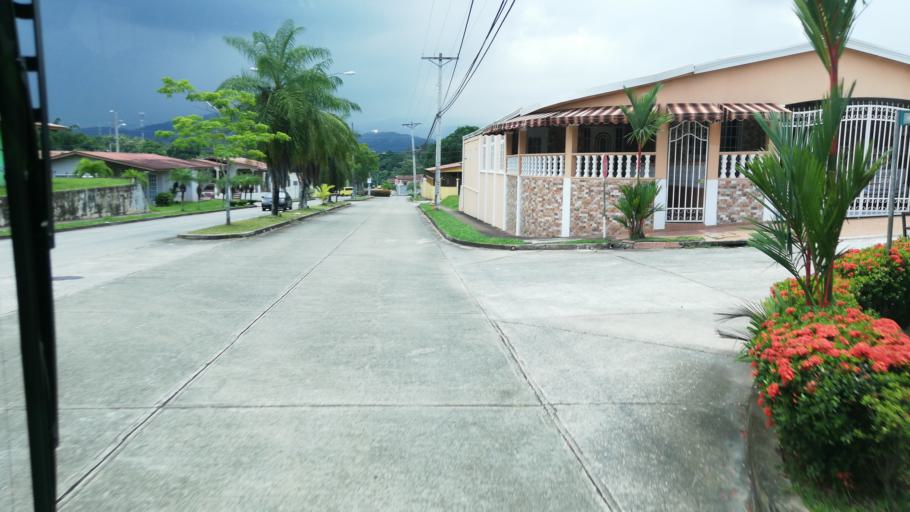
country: PA
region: Panama
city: San Miguelito
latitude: 9.0789
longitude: -79.4500
